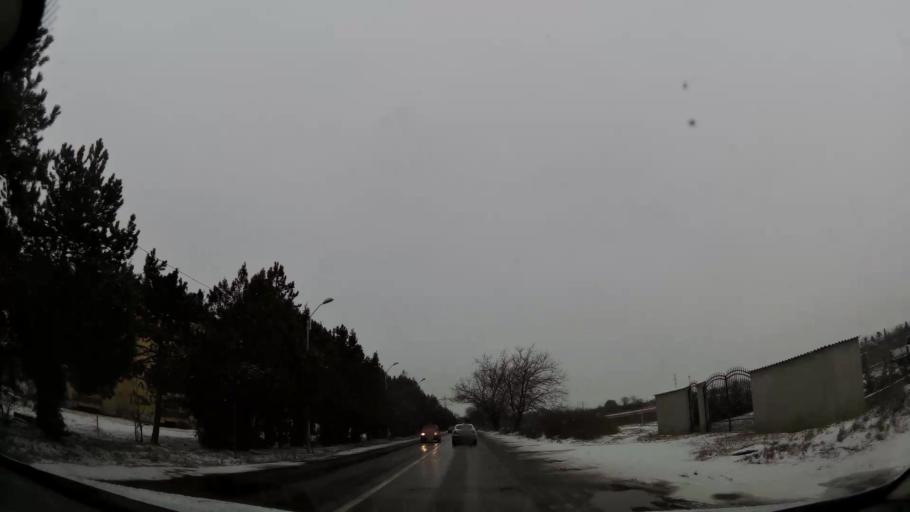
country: RO
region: Dambovita
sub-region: Comuna Ulmi
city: Ulmi
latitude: 44.9001
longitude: 25.5022
